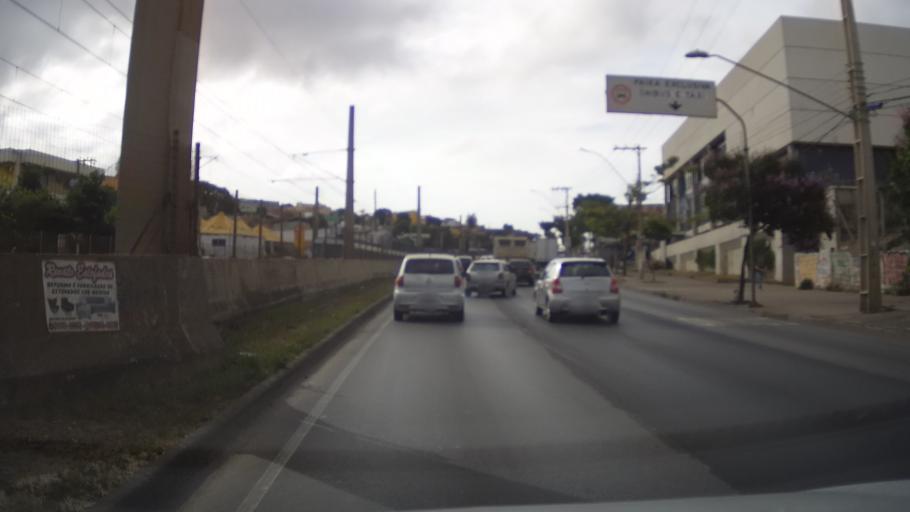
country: BR
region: Minas Gerais
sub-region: Belo Horizonte
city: Belo Horizonte
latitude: -19.8386
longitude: -43.9375
